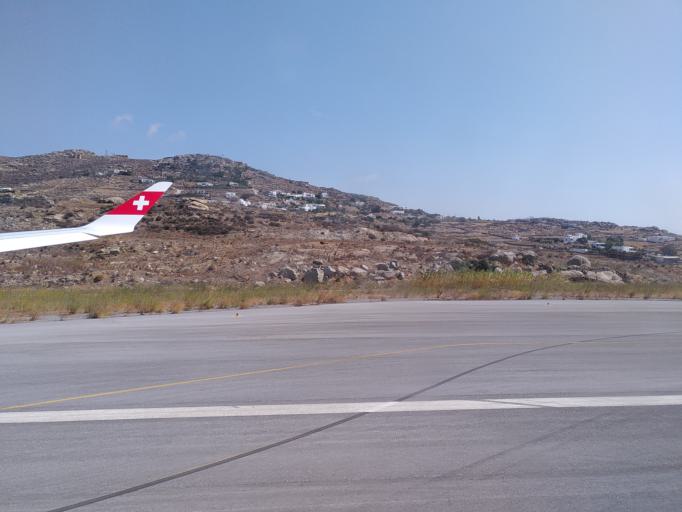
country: GR
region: South Aegean
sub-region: Nomos Kykladon
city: Mykonos
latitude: 37.4276
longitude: 25.3516
